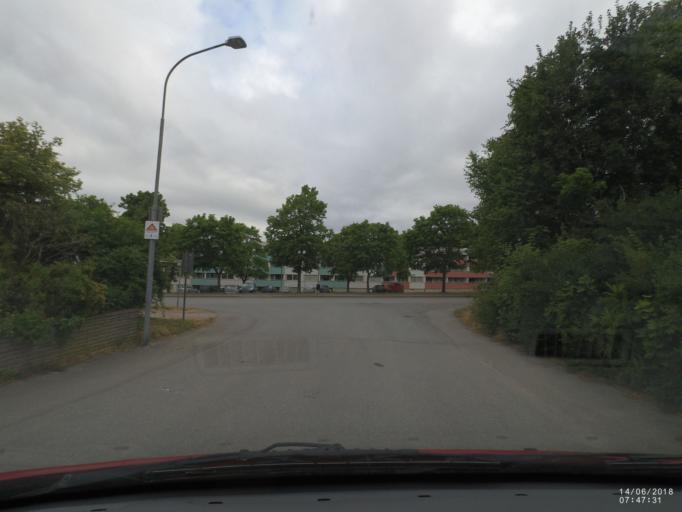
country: SE
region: Soedermanland
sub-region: Nykopings Kommun
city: Nykoping
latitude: 58.7650
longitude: 17.0118
